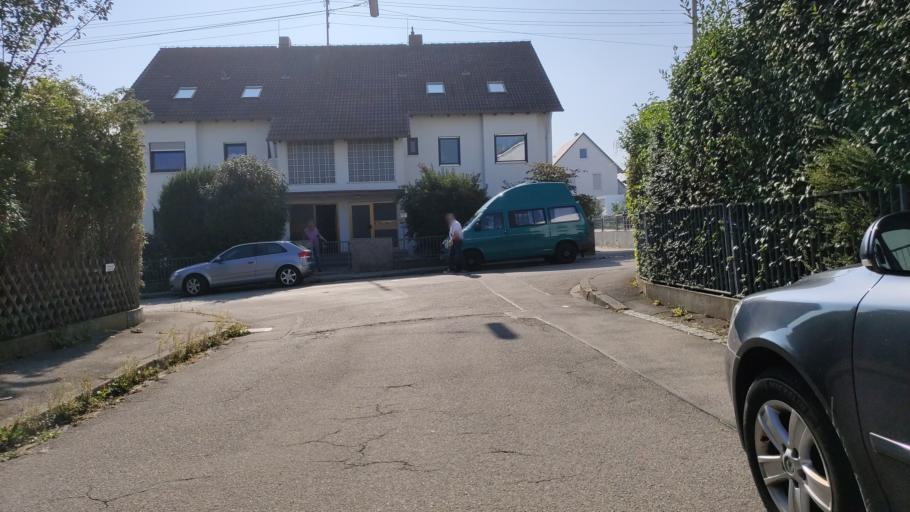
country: DE
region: Bavaria
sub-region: Swabia
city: Bobingen
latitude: 48.2746
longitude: 10.8428
